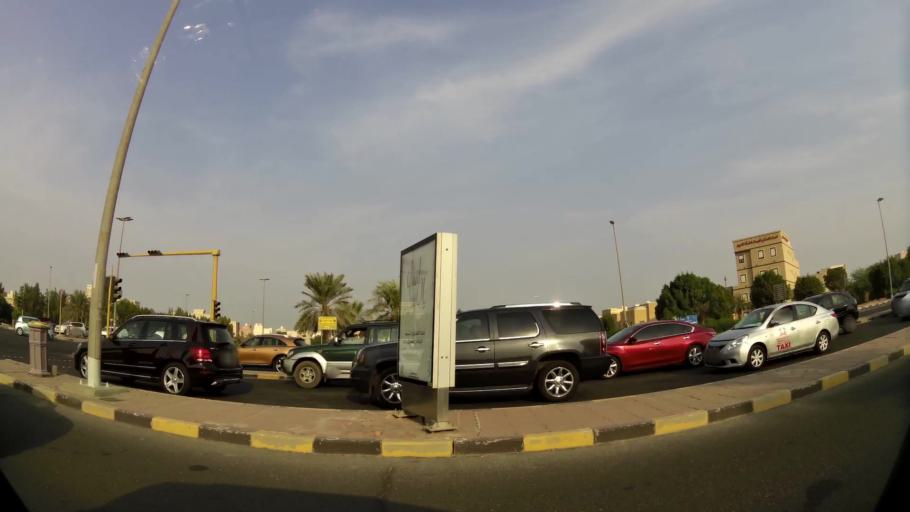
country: KW
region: Mubarak al Kabir
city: Mubarak al Kabir
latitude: 29.2078
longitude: 48.0691
